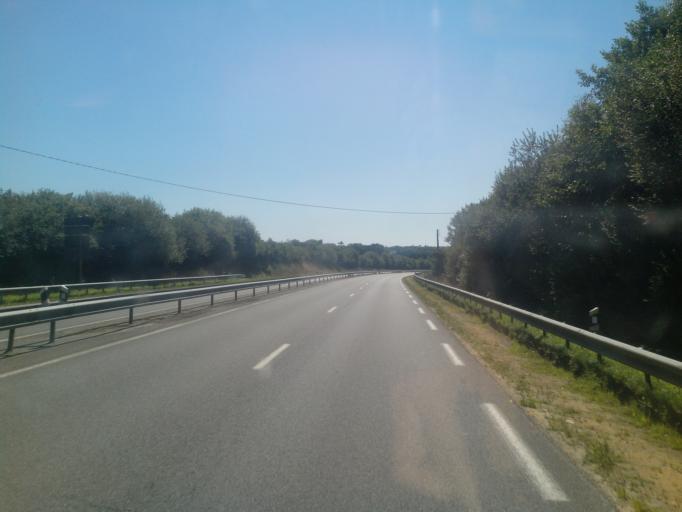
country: FR
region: Brittany
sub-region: Departement des Cotes-d'Armor
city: Saint-Brandan
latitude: 48.3224
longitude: -2.8295
